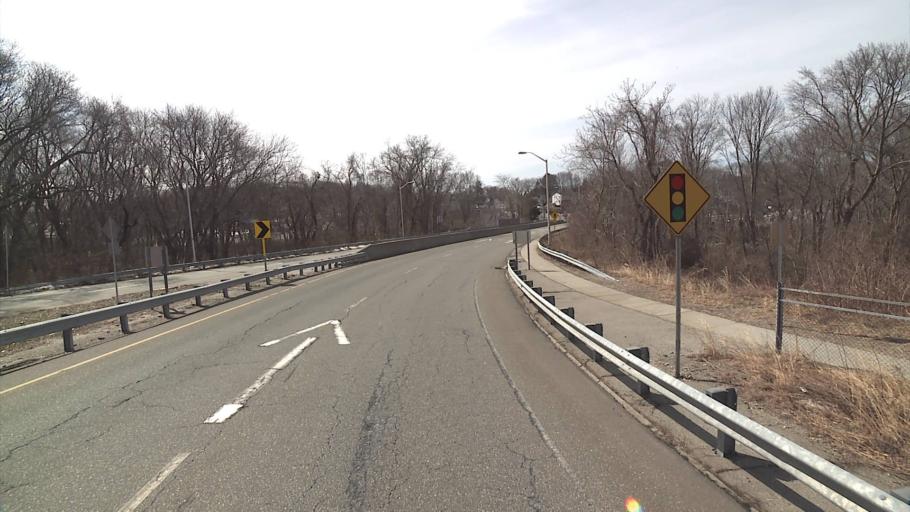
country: US
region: Connecticut
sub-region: New London County
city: Groton
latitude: 41.3630
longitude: -72.0763
